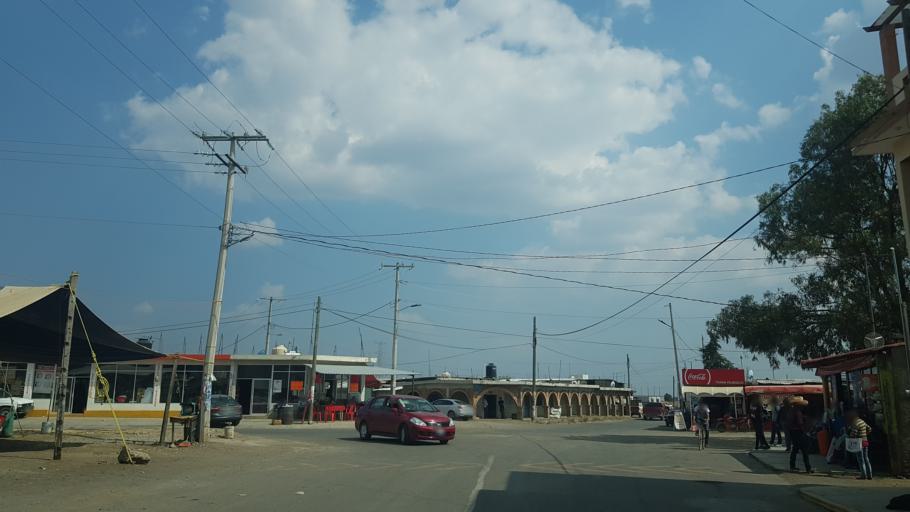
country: MX
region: Puebla
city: San Juan Amecac
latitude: 18.8269
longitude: -98.6559
